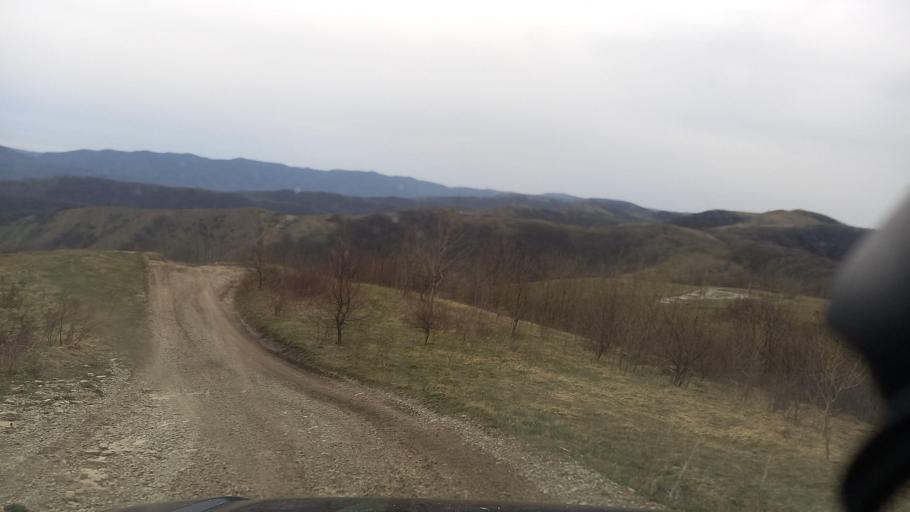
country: RU
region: Krasnodarskiy
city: Divnomorskoye
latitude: 44.6105
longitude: 38.2359
